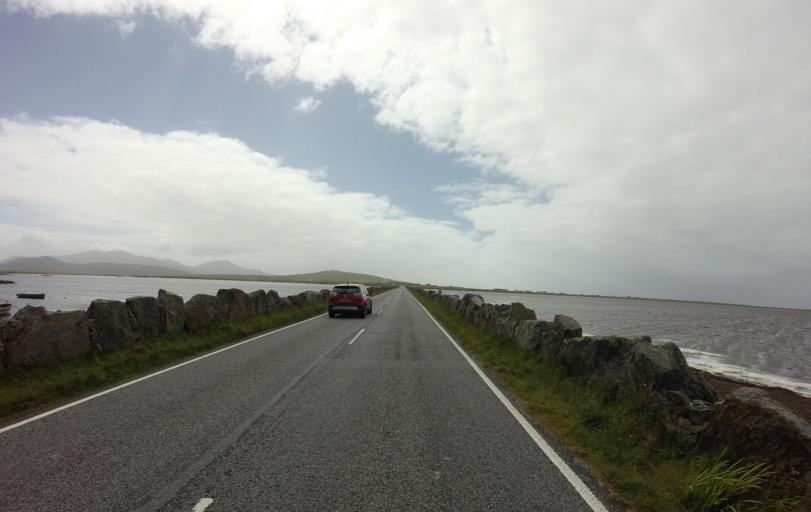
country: GB
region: Scotland
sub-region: Eilean Siar
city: Benbecula
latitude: 57.3630
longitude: -7.3546
